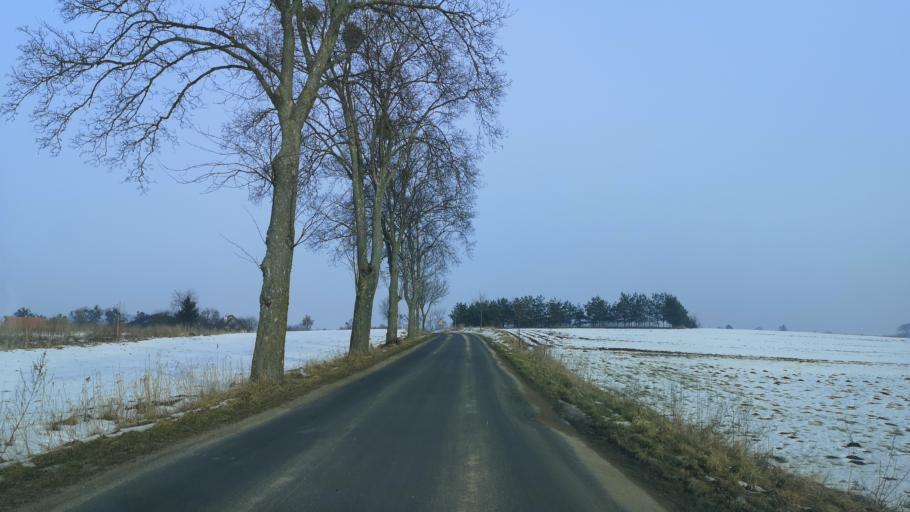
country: PL
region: Warmian-Masurian Voivodeship
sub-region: Powiat nowomiejski
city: Biskupiec
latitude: 53.4976
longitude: 19.3263
